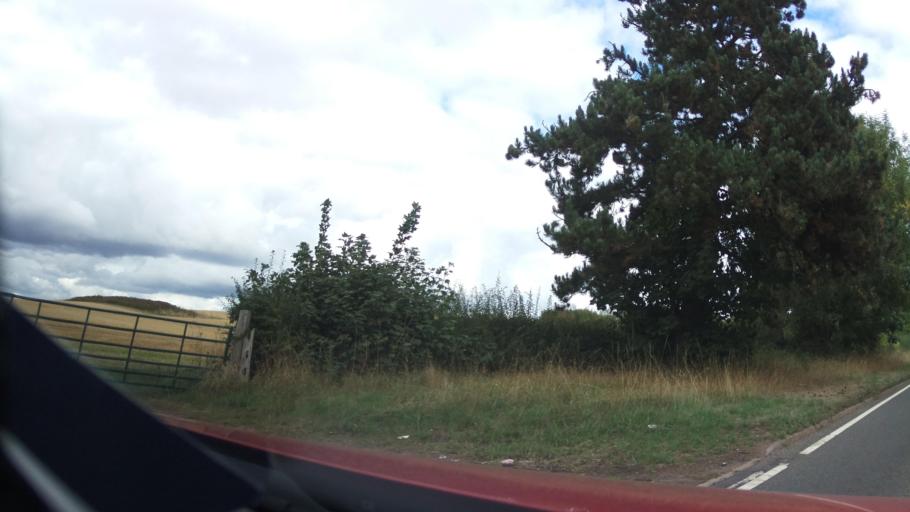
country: GB
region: England
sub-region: Leicestershire
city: Coalville
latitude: 52.7610
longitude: -1.3522
